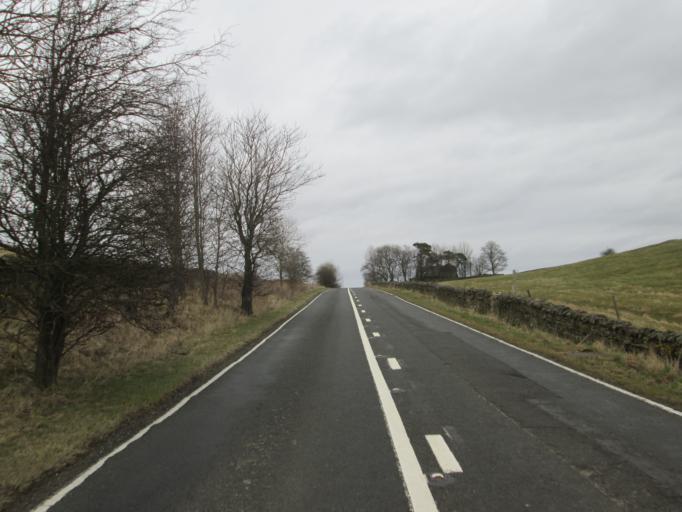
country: GB
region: England
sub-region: Northumberland
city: Haltwhistle
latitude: 54.9889
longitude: -2.4392
